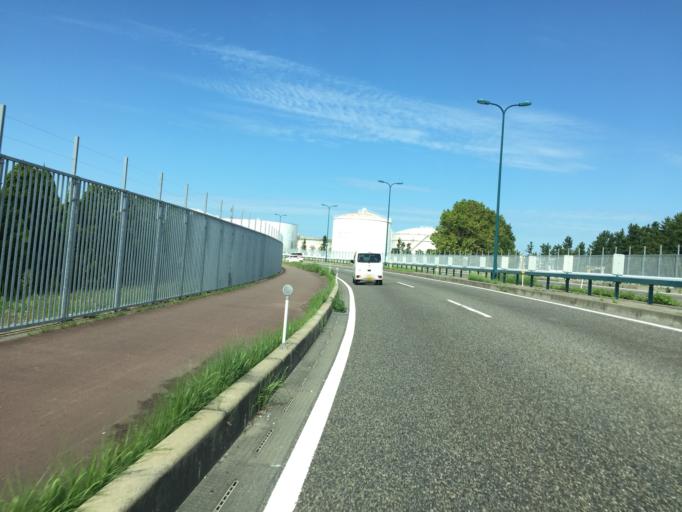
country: JP
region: Niigata
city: Niigata-shi
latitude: 37.9456
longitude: 139.0860
